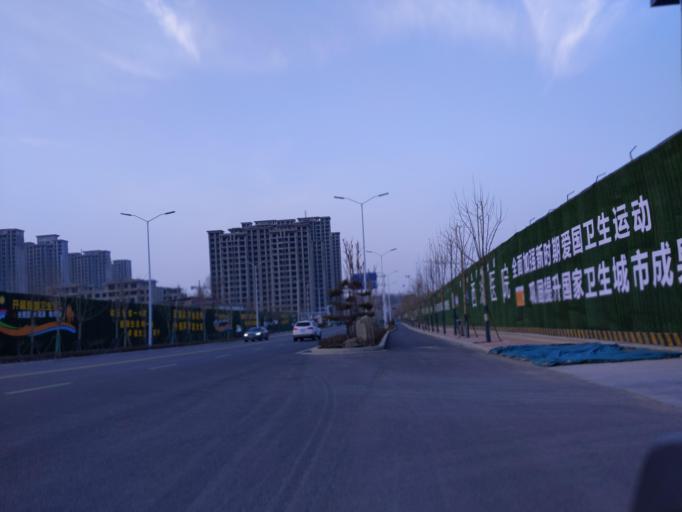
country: CN
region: Henan Sheng
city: Puyang
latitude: 35.8123
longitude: 115.0118
